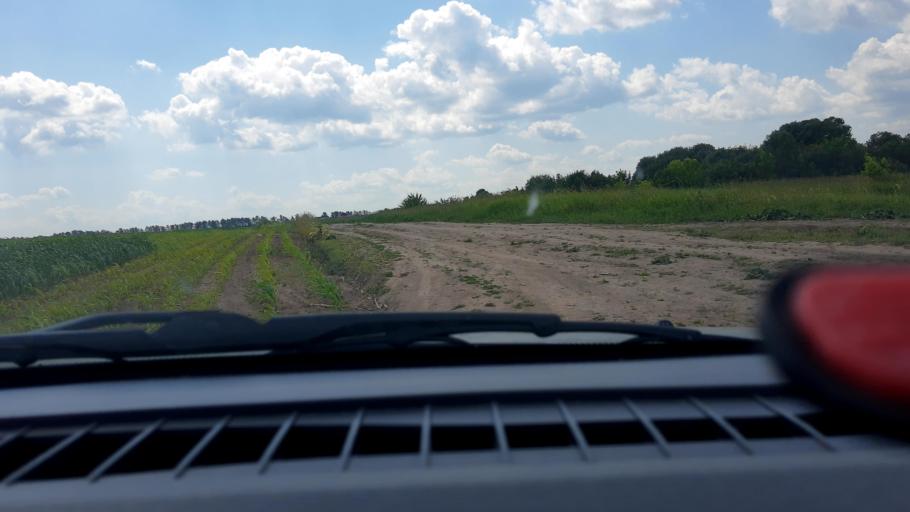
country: RU
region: Nizjnij Novgorod
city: Afonino
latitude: 56.1277
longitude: 44.0326
